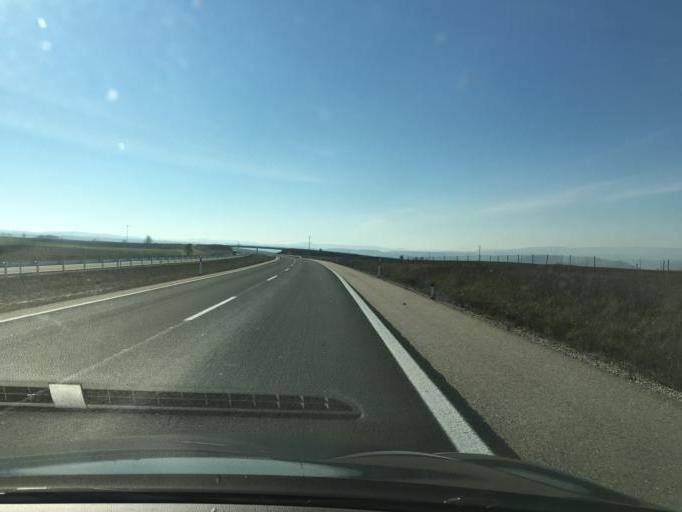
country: ES
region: Castille and Leon
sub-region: Provincia de Burgos
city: Grisalena
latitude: 42.5544
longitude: -3.2819
